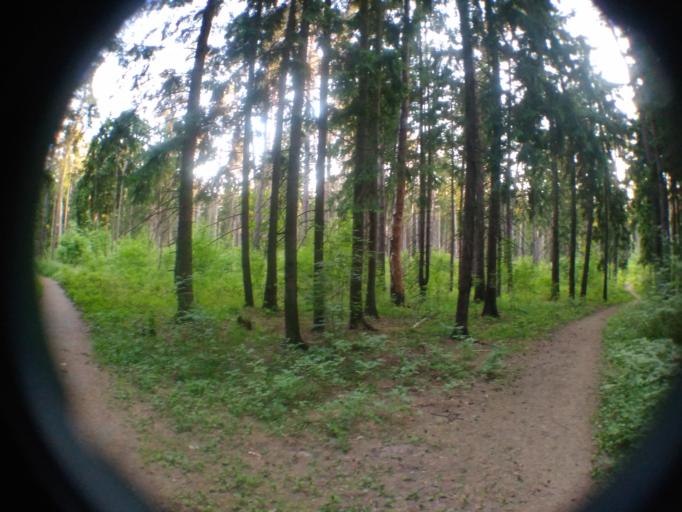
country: RU
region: Moskovskaya
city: Zhukovskiy
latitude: 55.5828
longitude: 38.1202
